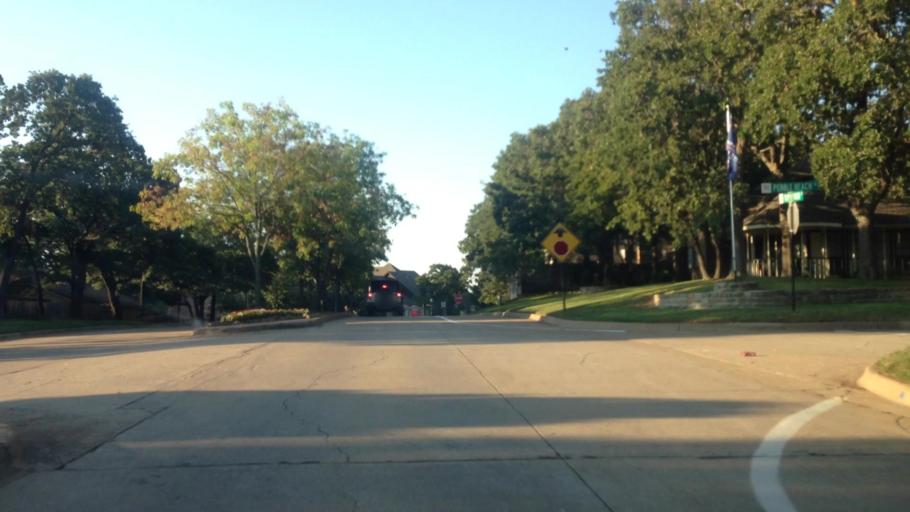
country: US
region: Texas
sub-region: Denton County
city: Trophy Club
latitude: 32.9905
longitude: -97.1692
